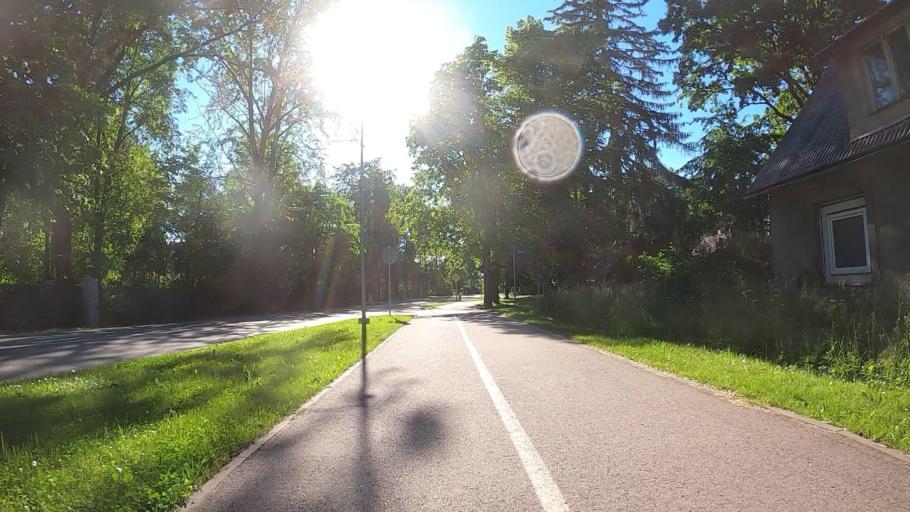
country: LV
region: Ogre
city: Ogre
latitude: 56.8125
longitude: 24.6368
